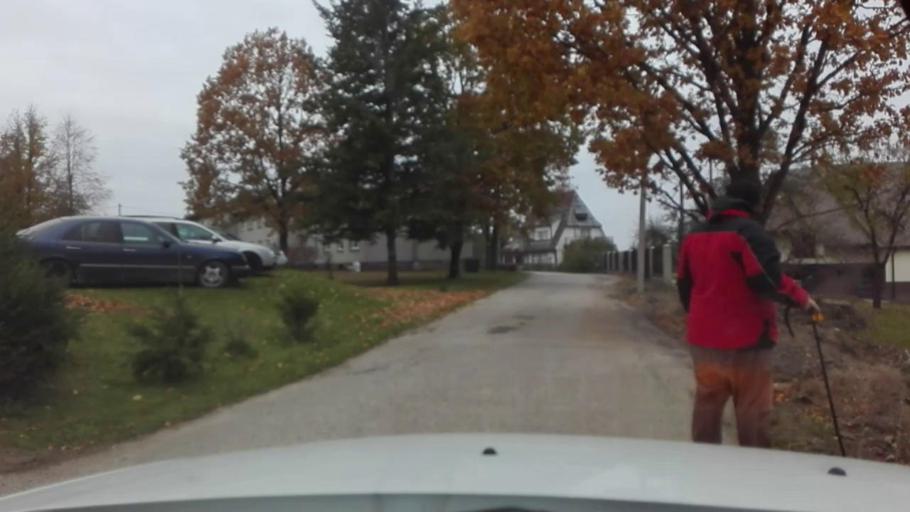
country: EE
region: Jogevamaa
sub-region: Poltsamaa linn
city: Poltsamaa
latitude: 58.5340
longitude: 25.9453
